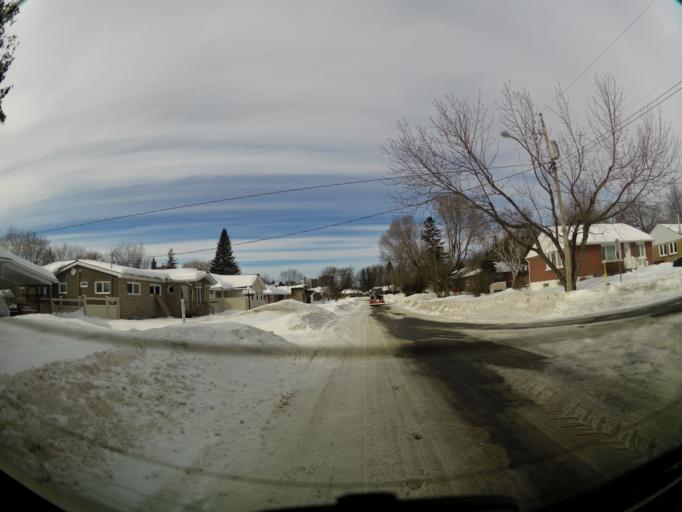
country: CA
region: Ontario
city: Ottawa
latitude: 45.4409
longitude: -75.6096
